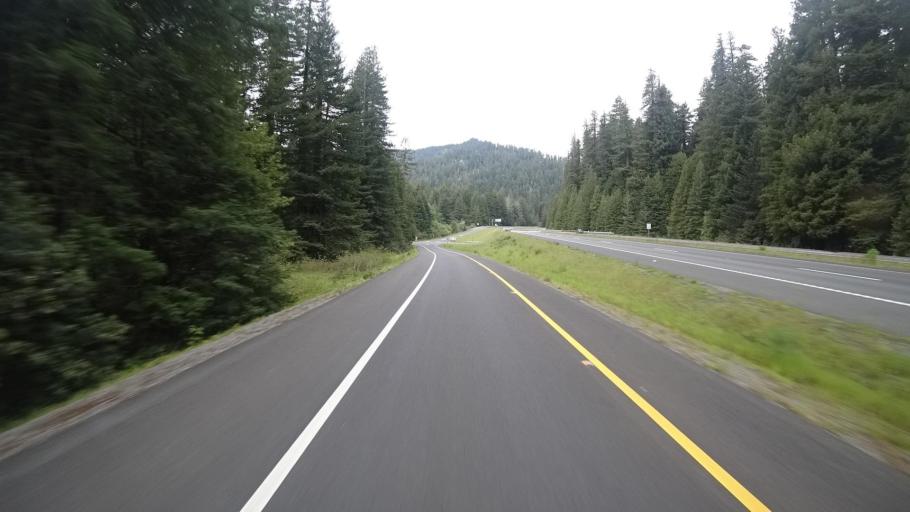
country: US
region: California
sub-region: Humboldt County
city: Rio Dell
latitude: 40.4397
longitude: -124.0306
